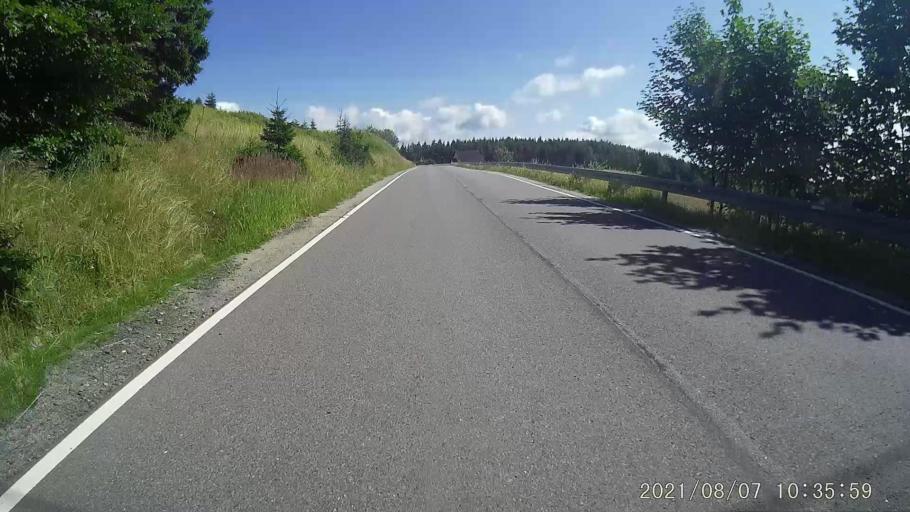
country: PL
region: Lower Silesian Voivodeship
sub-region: Powiat klodzki
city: Duszniki-Zdroj
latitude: 50.3649
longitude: 16.3708
